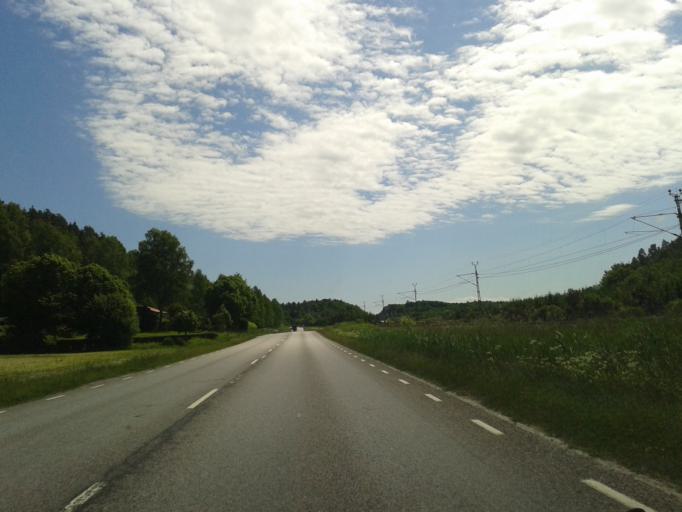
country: SE
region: Vaestra Goetaland
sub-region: Uddevalla Kommun
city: Ljungskile
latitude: 58.2699
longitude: 11.8931
